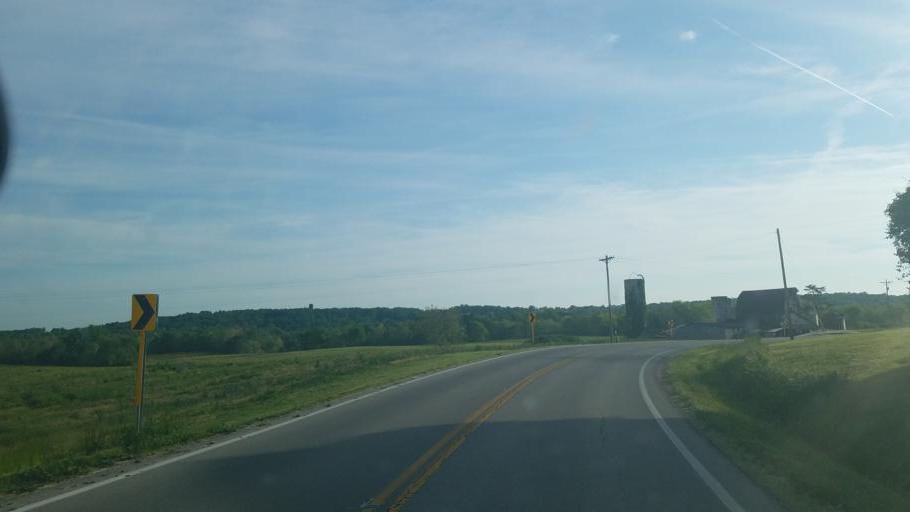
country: US
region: Ohio
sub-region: Ross County
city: Frankfort
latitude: 39.4074
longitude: -83.2814
